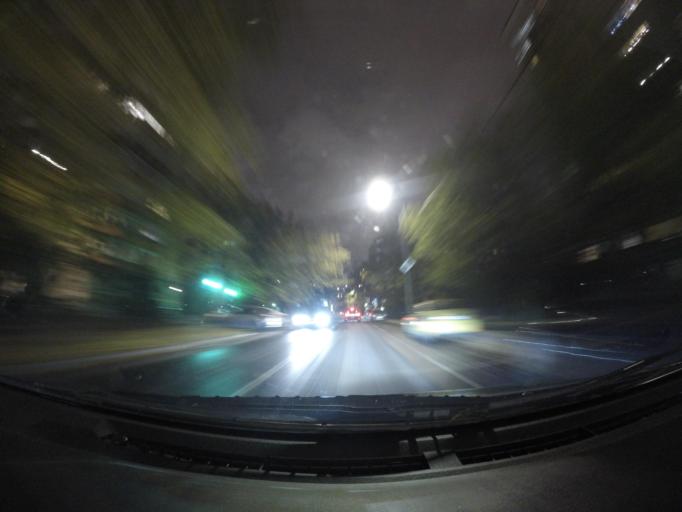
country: RU
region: Moscow
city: Likhobory
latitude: 55.8231
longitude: 37.5696
